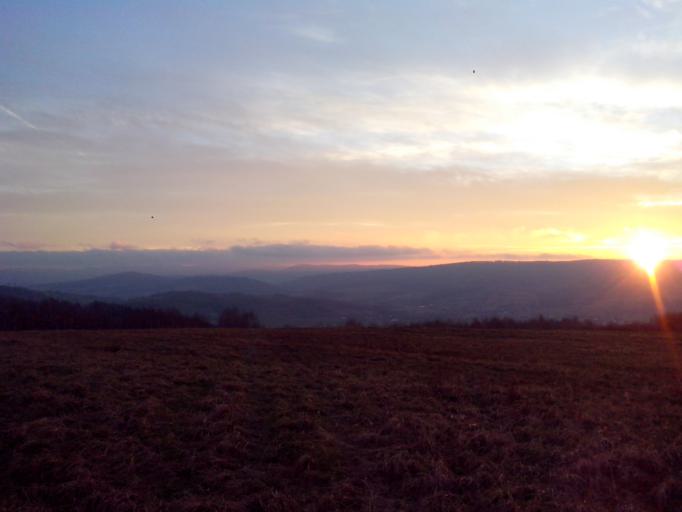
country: PL
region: Subcarpathian Voivodeship
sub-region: Powiat strzyzowski
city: Jawornik
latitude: 49.8488
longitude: 21.8476
